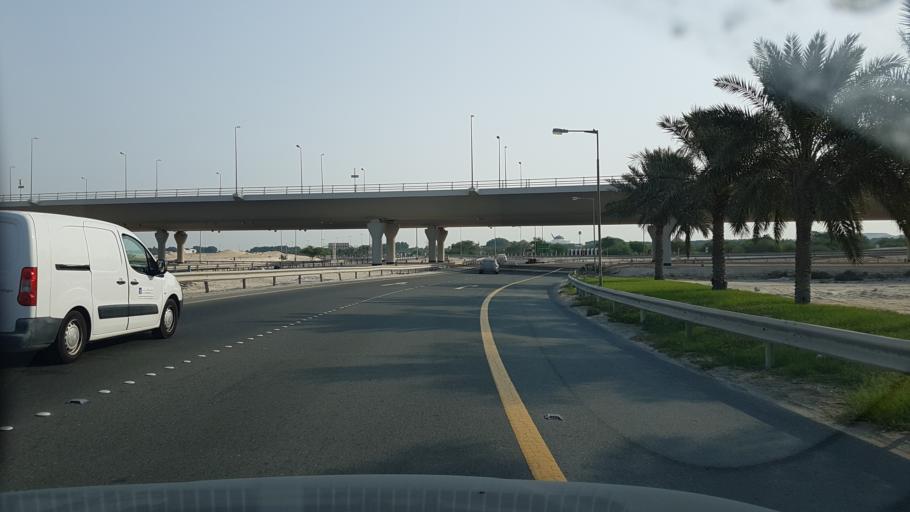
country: BH
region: Central Governorate
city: Dar Kulayb
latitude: 26.0589
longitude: 50.5169
